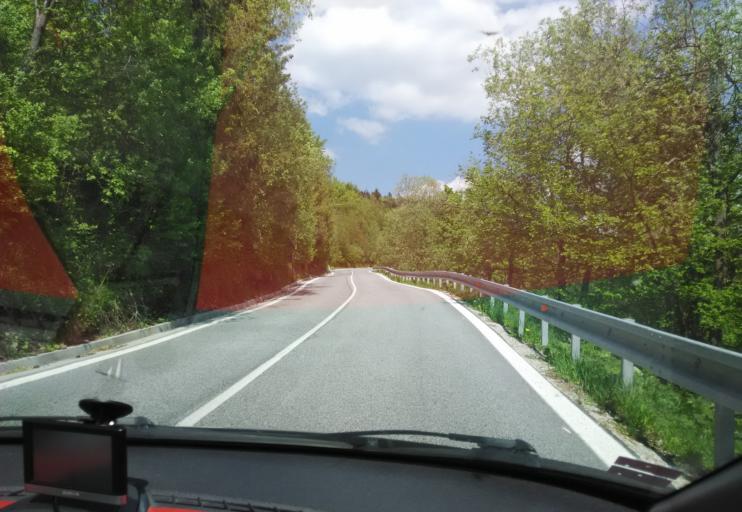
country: SK
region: Kosicky
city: Dobsina
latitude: 48.8440
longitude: 20.4379
